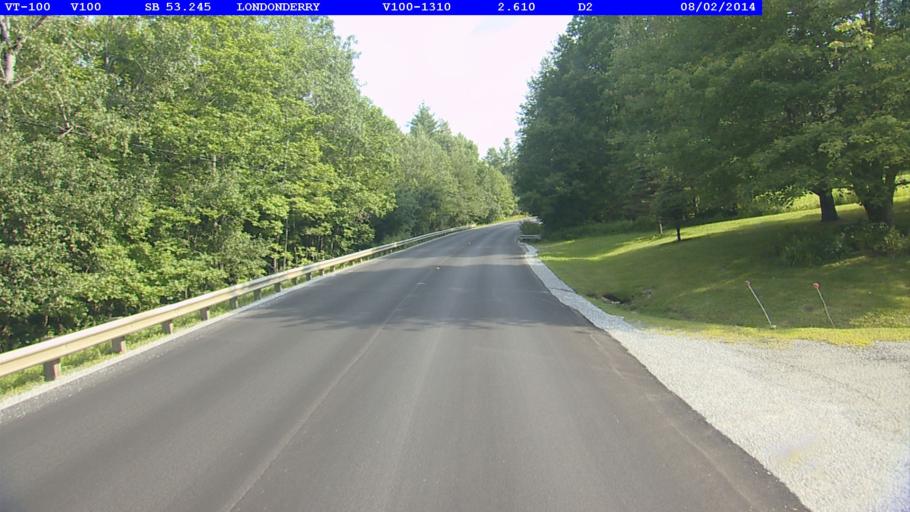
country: US
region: Vermont
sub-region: Windsor County
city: Chester
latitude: 43.1875
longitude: -72.8133
